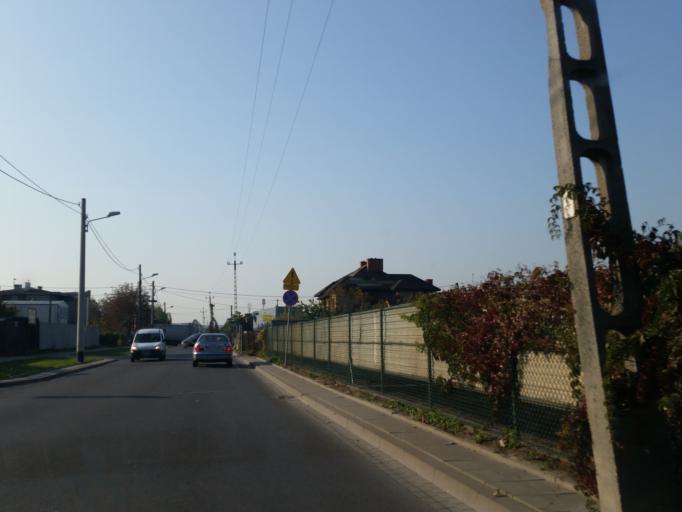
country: PL
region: Masovian Voivodeship
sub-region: Warszawa
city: Wlochy
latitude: 52.1805
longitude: 20.9393
